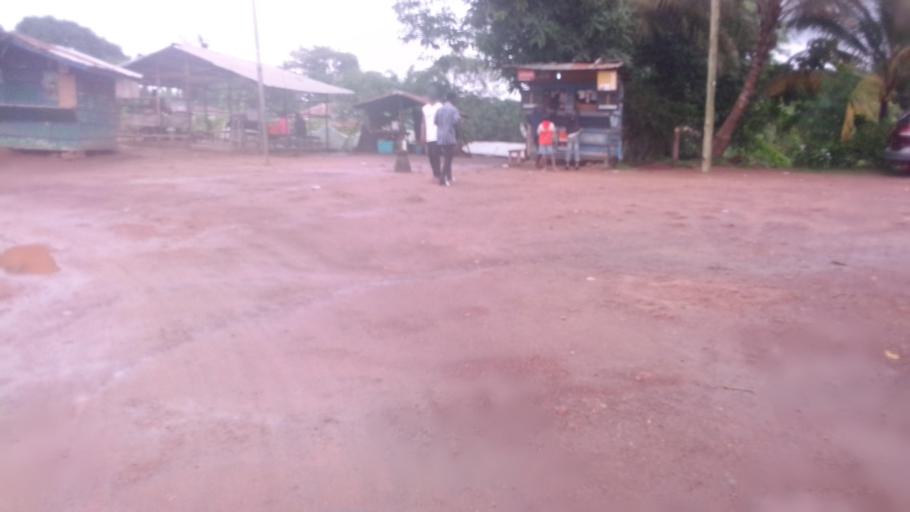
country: SL
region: Eastern Province
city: Kenema
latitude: 7.8873
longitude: -11.1754
